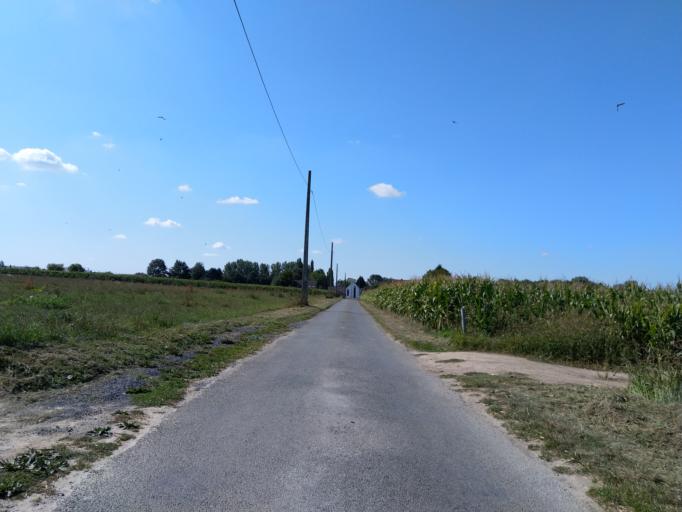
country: BE
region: Wallonia
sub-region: Province du Hainaut
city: Jurbise
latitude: 50.5251
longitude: 3.8660
